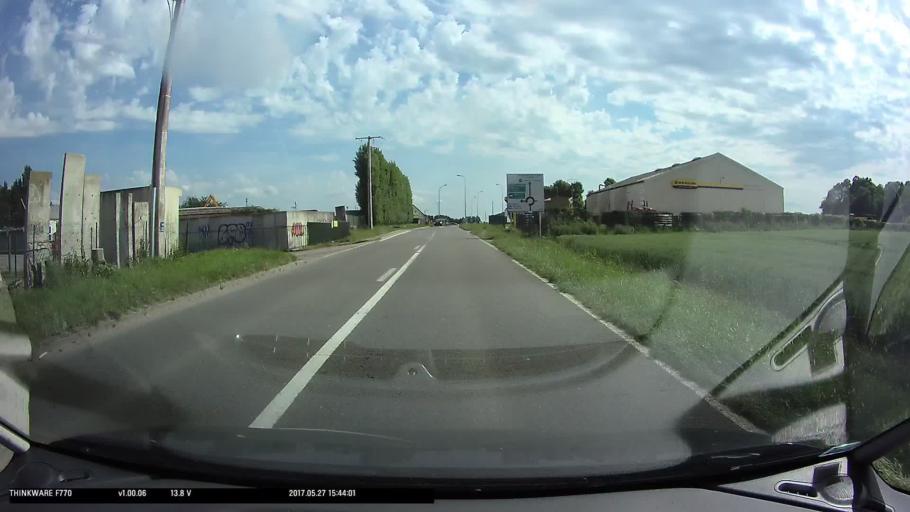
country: FR
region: Ile-de-France
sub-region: Departement du Val-d'Oise
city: Chars
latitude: 49.1967
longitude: 1.8798
